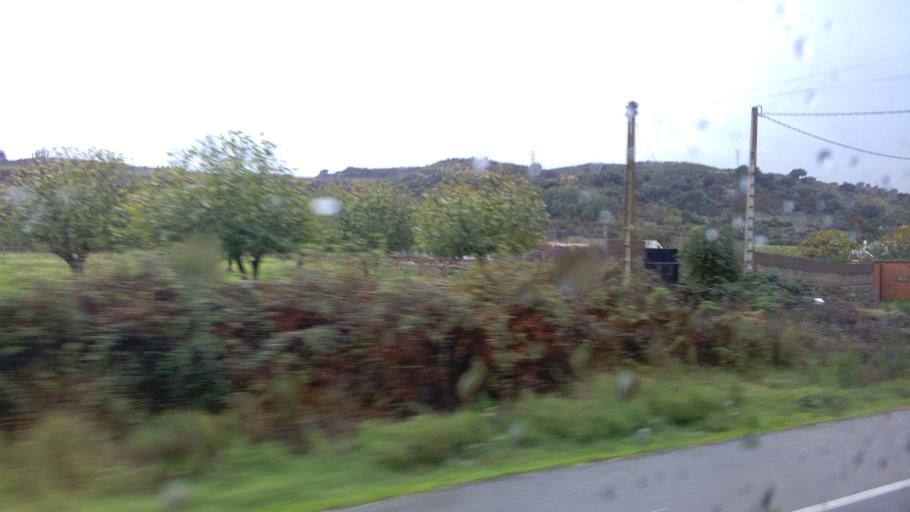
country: ES
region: Extremadura
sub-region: Provincia de Caceres
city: Navalmoral de la Mata
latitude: 39.8914
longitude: -5.5188
